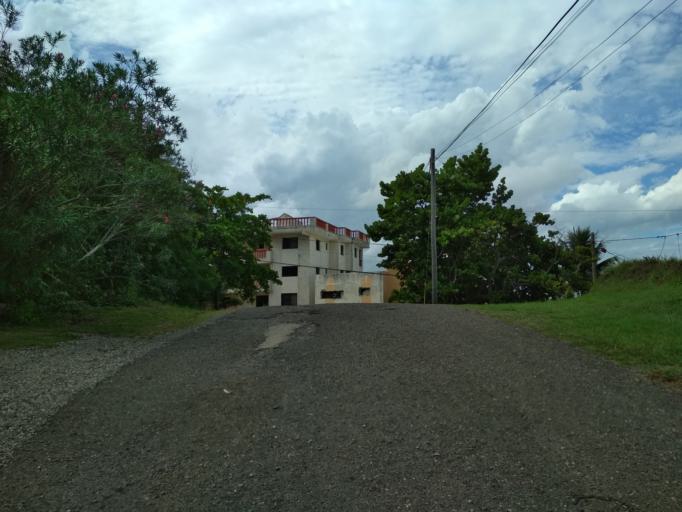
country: DO
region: Puerto Plata
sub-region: Puerto Plata
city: Puerto Plata
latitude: 19.8089
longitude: -70.7098
